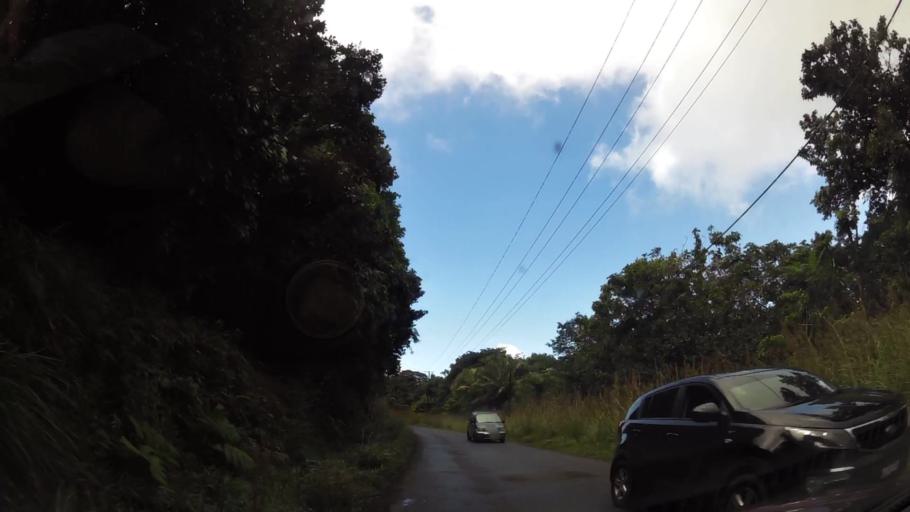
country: DM
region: Saint Paul
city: Pont Casse
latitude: 15.3922
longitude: -61.3277
